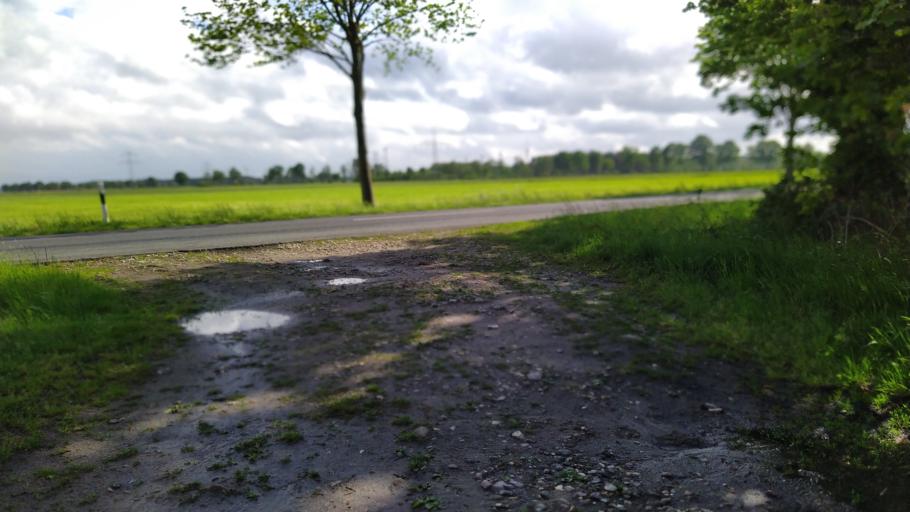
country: DE
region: Lower Saxony
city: Brest
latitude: 53.4533
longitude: 9.4024
